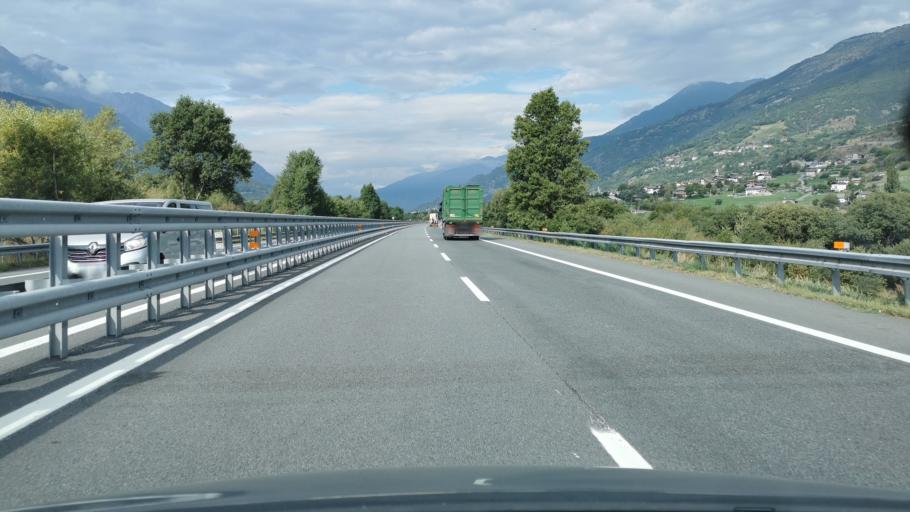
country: IT
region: Aosta Valley
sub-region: Valle d'Aosta
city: Chambave
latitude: 45.7418
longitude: 7.5360
